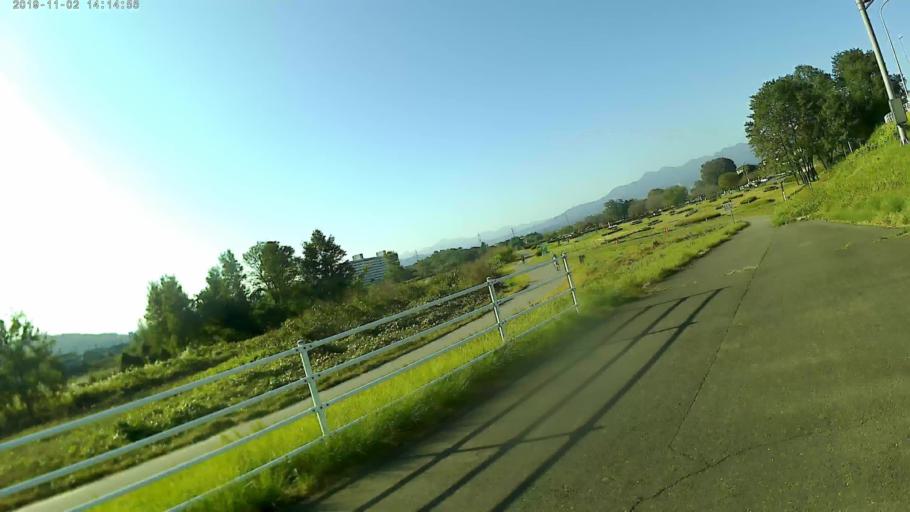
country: JP
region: Gunma
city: Takasaki
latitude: 36.3345
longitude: 138.9905
